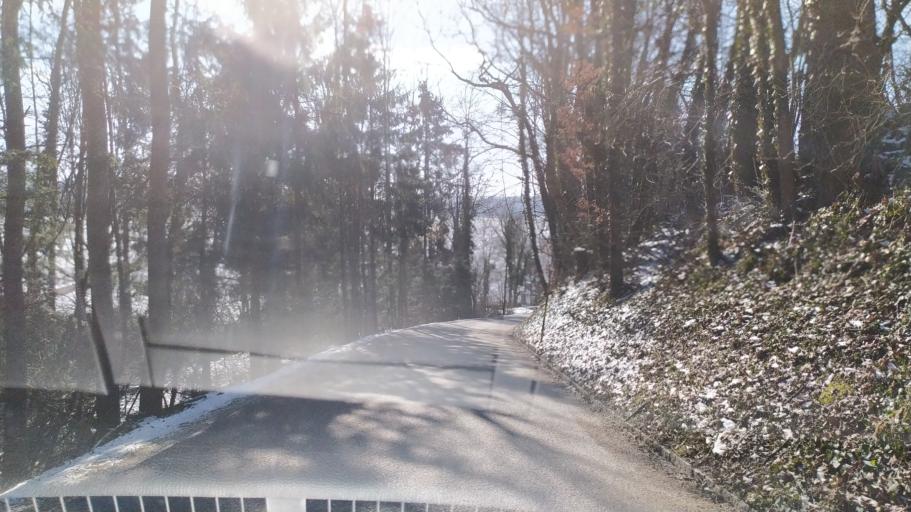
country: AT
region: Upper Austria
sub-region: Politischer Bezirk Urfahr-Umgebung
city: Ottensheim
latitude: 48.3365
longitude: 14.1935
